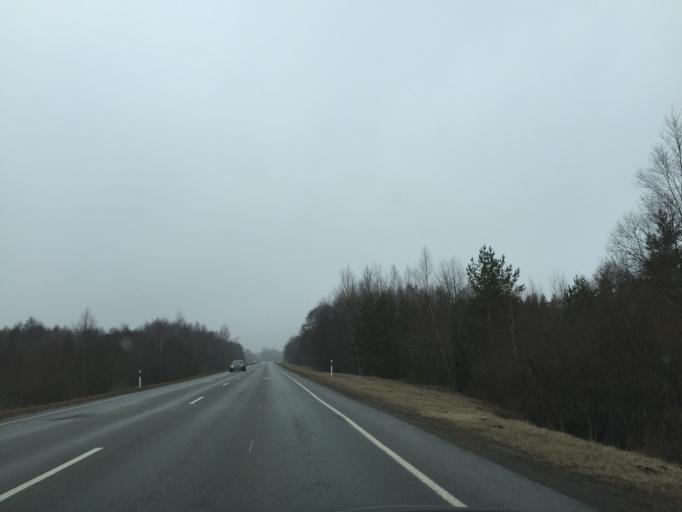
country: EE
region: Laeaene
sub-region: Lihula vald
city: Lihula
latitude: 58.5951
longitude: 23.5454
